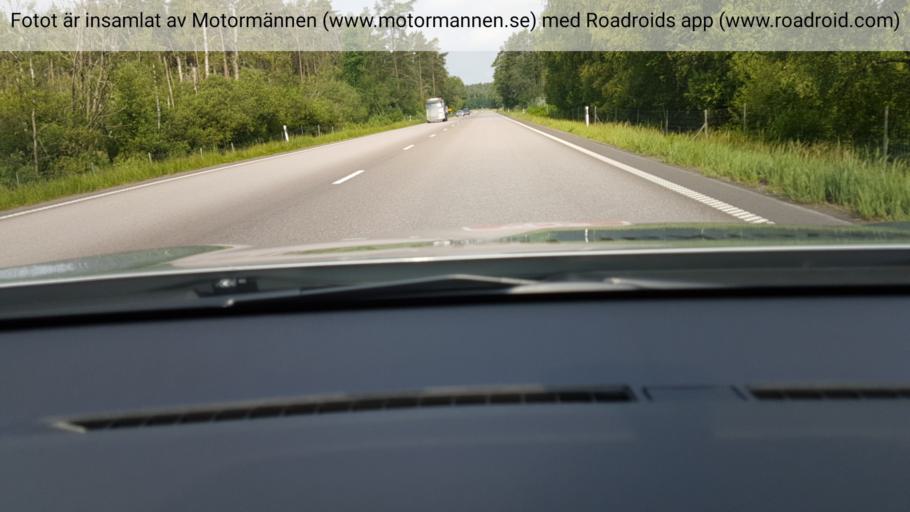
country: SE
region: Vaestra Goetaland
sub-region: Lidkopings Kommun
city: Vinninga
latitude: 58.4243
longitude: 13.3348
